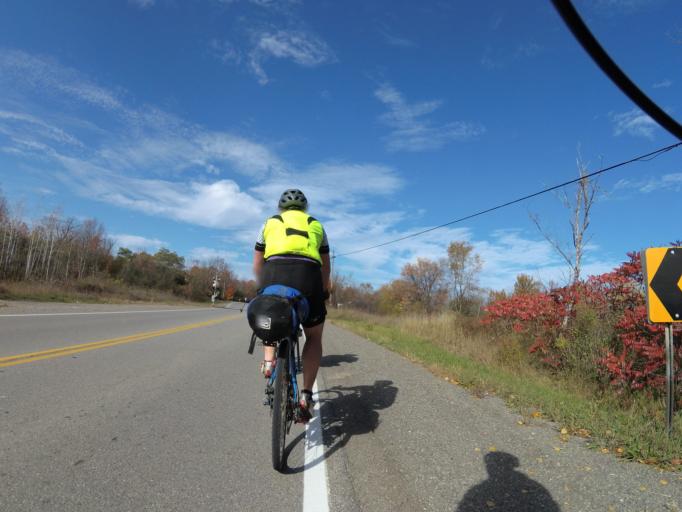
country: CA
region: Ontario
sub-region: Lanark County
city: Smiths Falls
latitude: 44.8958
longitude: -76.0166
